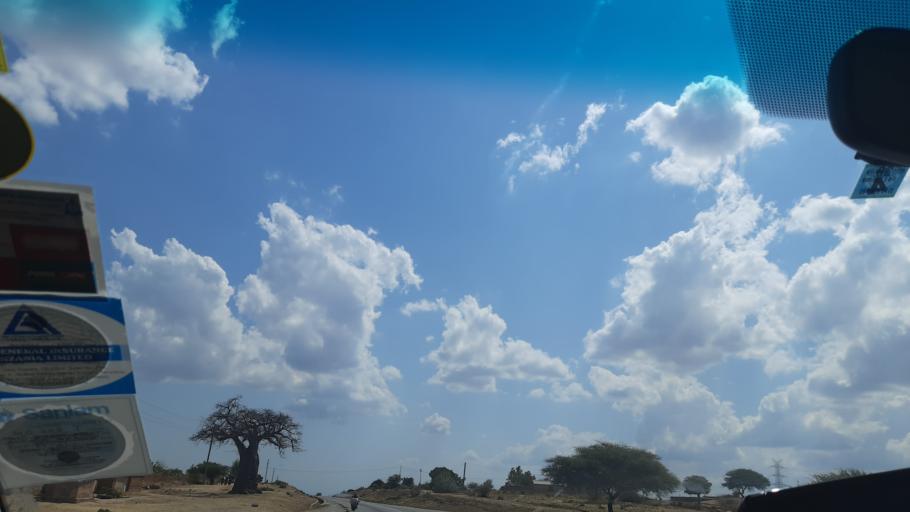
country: TZ
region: Singida
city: Kintinku
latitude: -6.0173
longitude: 35.4483
